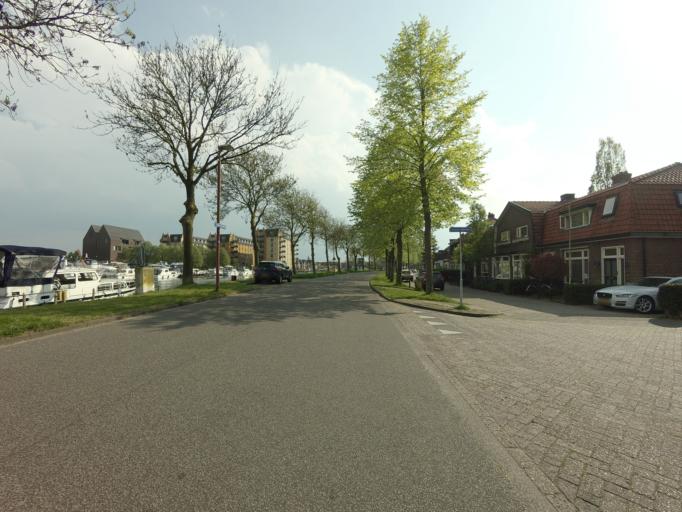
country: NL
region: Utrecht
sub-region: Gemeente Vianen
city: Vianen
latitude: 52.0138
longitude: 5.0976
